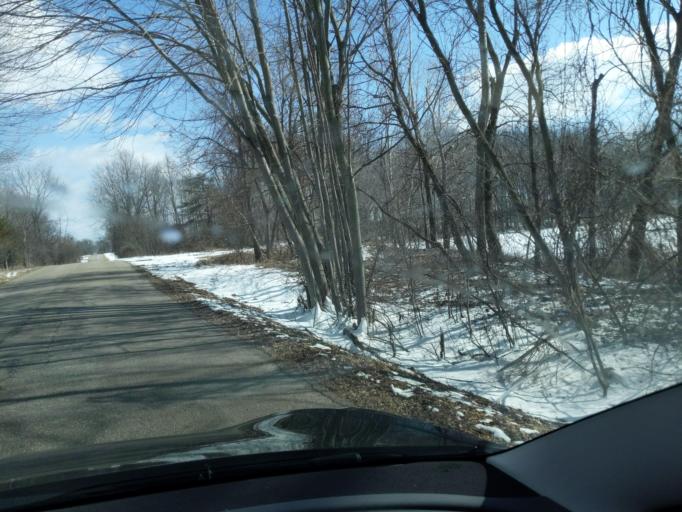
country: US
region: Michigan
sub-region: Ingham County
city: Webberville
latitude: 42.6153
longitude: -84.2227
